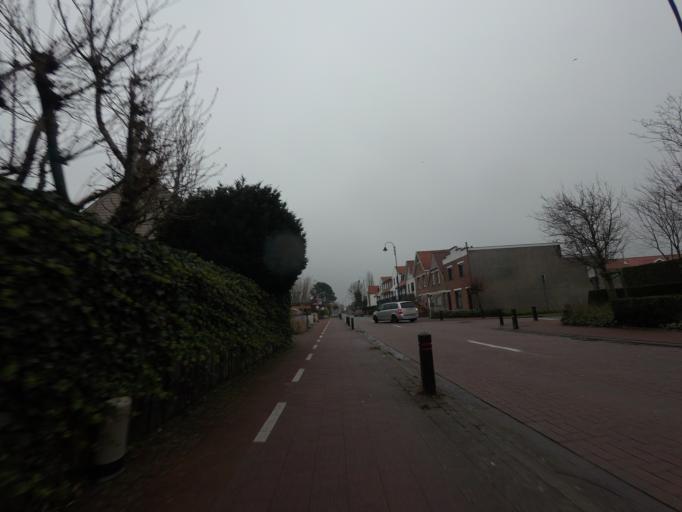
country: BE
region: Flanders
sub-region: Provincie West-Vlaanderen
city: Knokke-Heist
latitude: 51.3334
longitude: 3.2967
